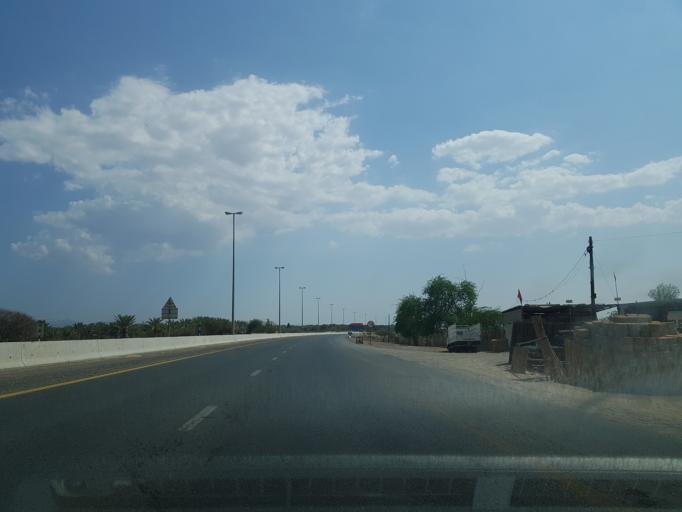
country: AE
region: Ash Shariqah
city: Adh Dhayd
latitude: 25.2411
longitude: 55.9151
